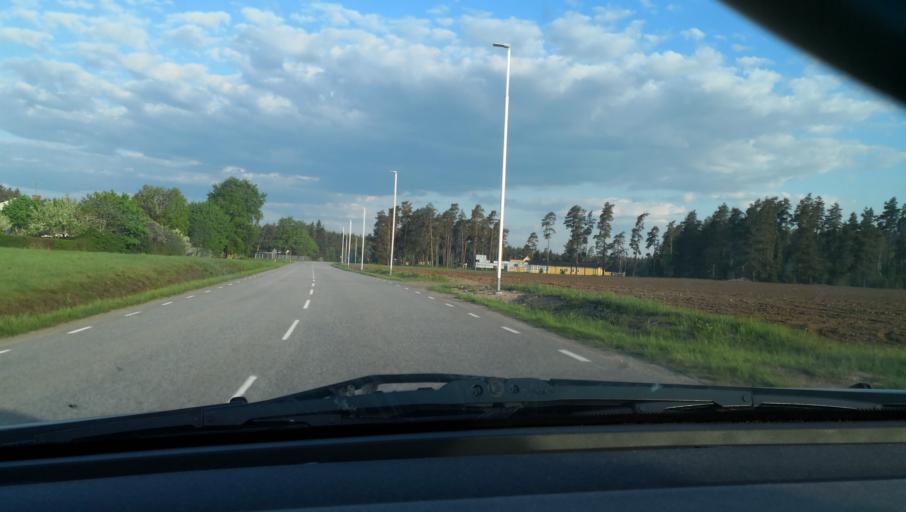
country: SE
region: Joenkoeping
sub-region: Vetlanda Kommun
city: Landsbro
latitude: 57.3740
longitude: 14.8883
